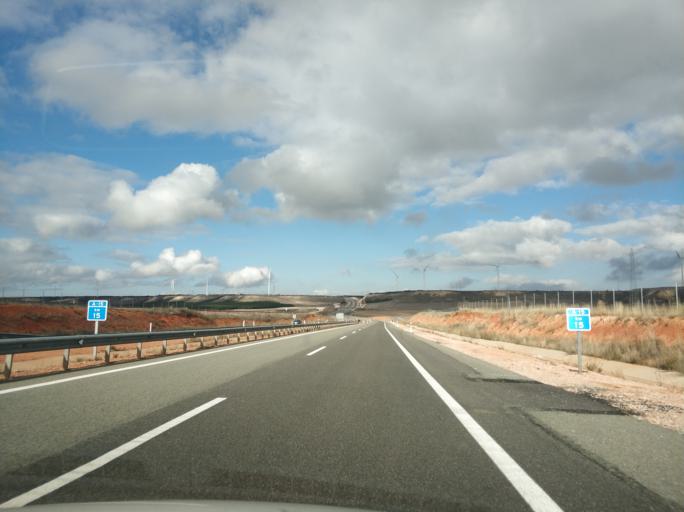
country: ES
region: Castille and Leon
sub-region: Provincia de Soria
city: Alcubilla de las Penas
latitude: 41.2720
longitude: -2.4742
